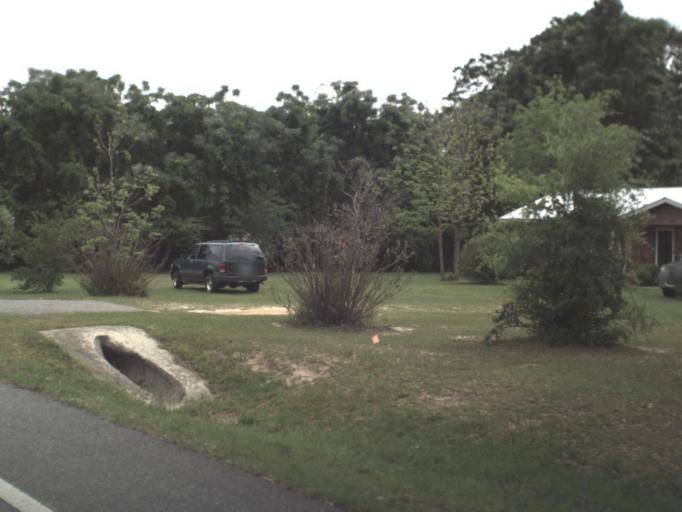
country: US
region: Florida
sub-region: Santa Rosa County
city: Point Baker
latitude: 30.8305
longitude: -87.0483
